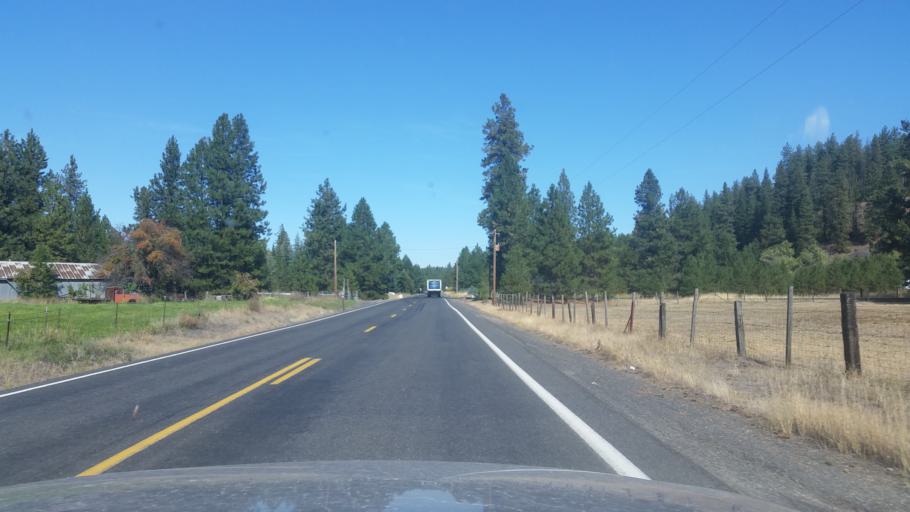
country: US
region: Washington
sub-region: Spokane County
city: Spokane
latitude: 47.5791
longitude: -117.4617
